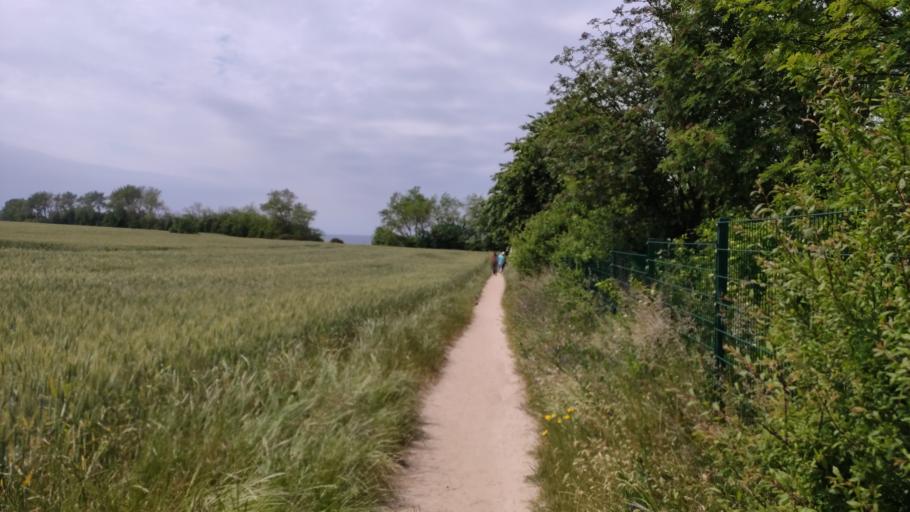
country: DE
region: Mecklenburg-Vorpommern
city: Bastorf
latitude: 54.1274
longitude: 11.6438
